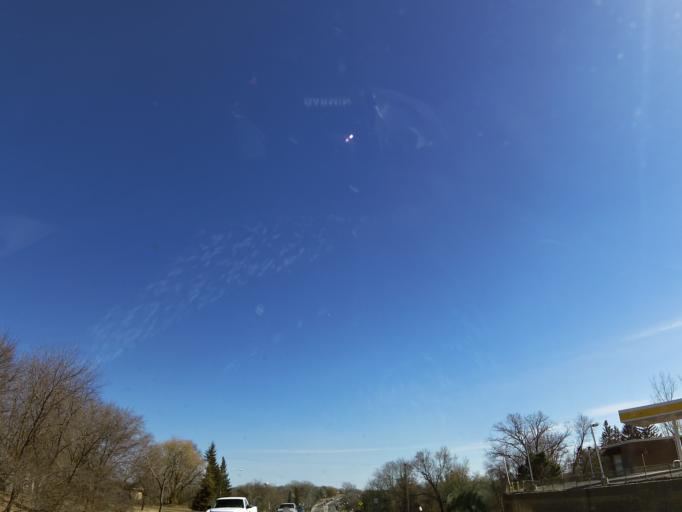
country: US
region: Minnesota
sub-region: Wright County
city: Rockford
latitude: 45.0894
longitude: -93.7410
